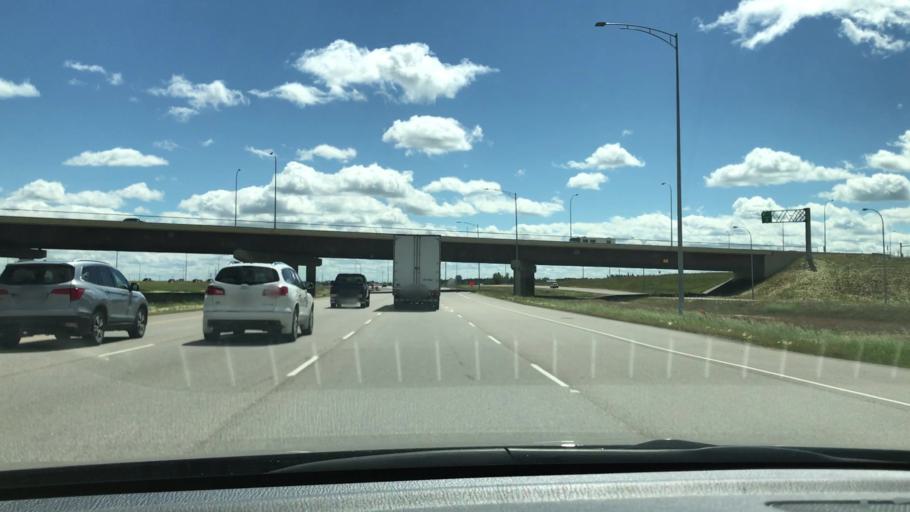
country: CA
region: Alberta
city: Beaumont
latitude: 53.3978
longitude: -113.5115
